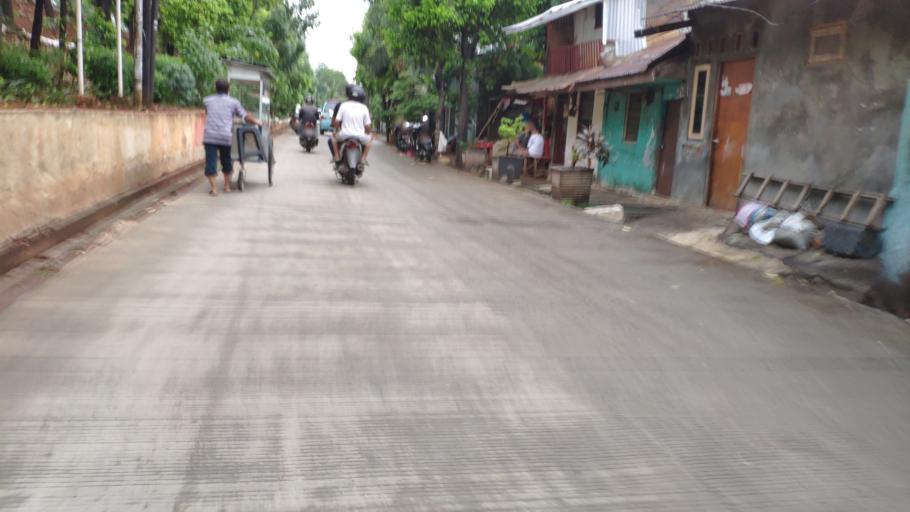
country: ID
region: Jakarta Raya
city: Jakarta
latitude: -6.2130
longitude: 106.8737
